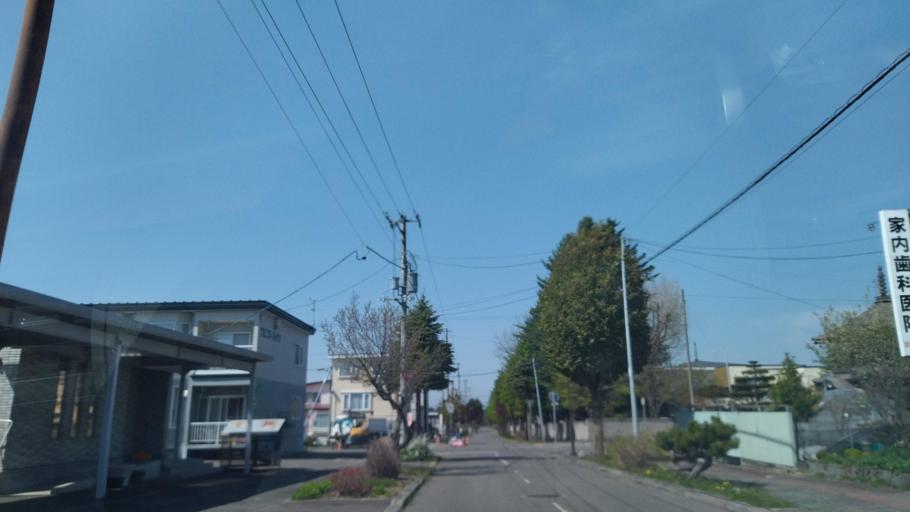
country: JP
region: Hokkaido
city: Obihiro
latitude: 42.9112
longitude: 143.0452
